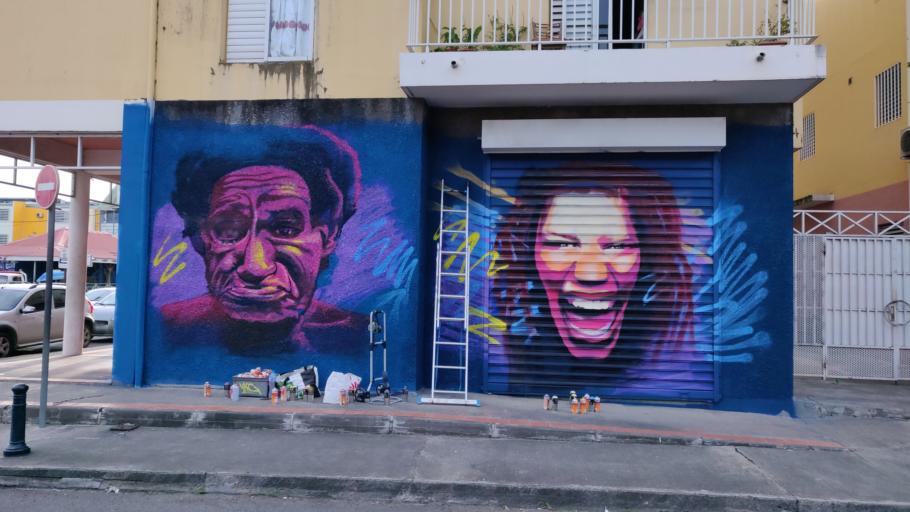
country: GP
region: Guadeloupe
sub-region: Guadeloupe
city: Pointe-a-Pitre
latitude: 16.2349
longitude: -61.5331
